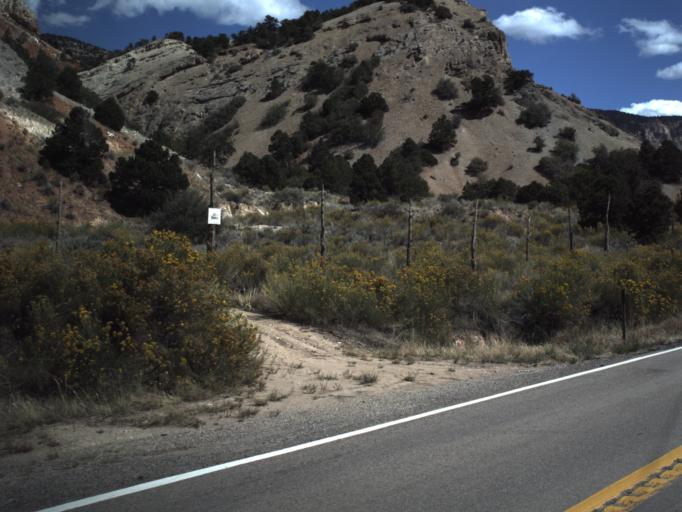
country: US
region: Utah
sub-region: Iron County
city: Cedar City
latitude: 37.6734
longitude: -113.0263
